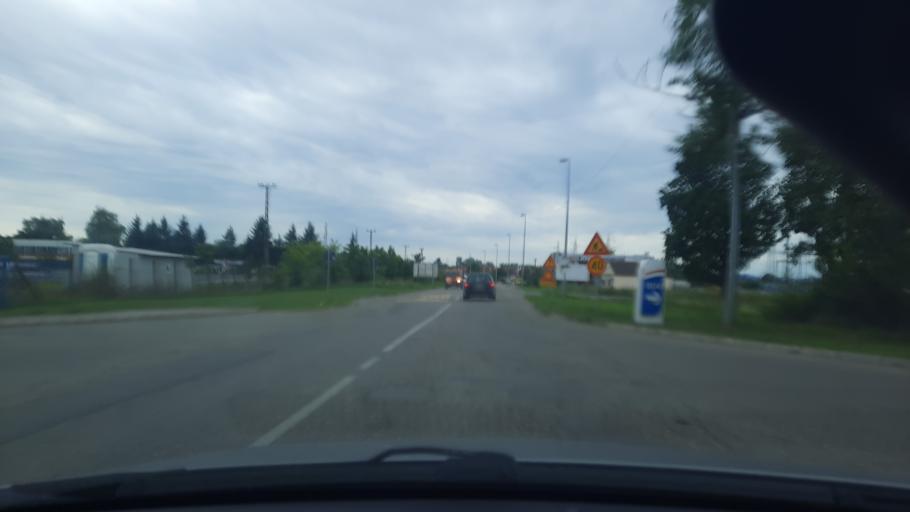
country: RS
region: Central Serbia
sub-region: Macvanski Okrug
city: Sabac
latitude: 44.7390
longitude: 19.6743
